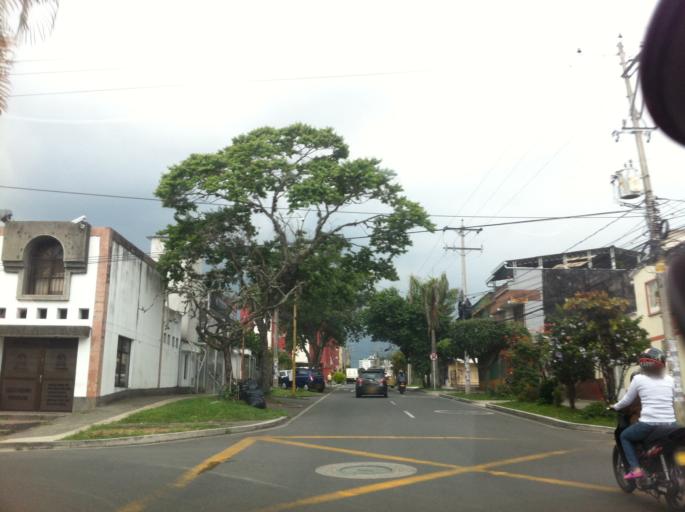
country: CO
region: Quindio
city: Armenia
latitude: 4.5413
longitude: -75.6678
